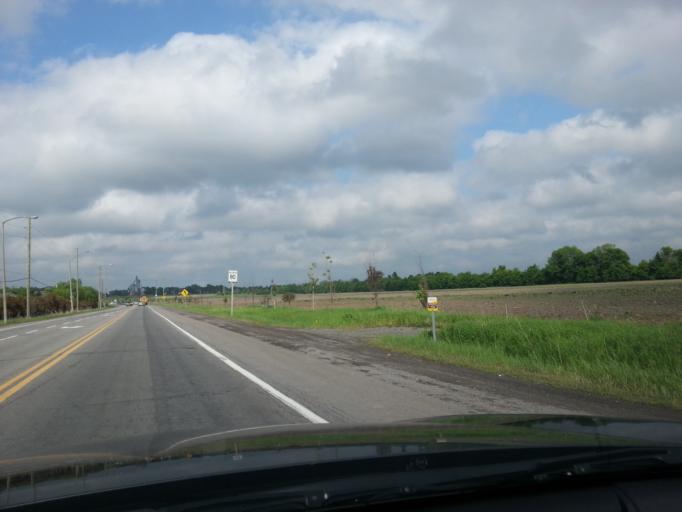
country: CA
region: Ontario
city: Bells Corners
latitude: 45.2599
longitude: -75.8253
